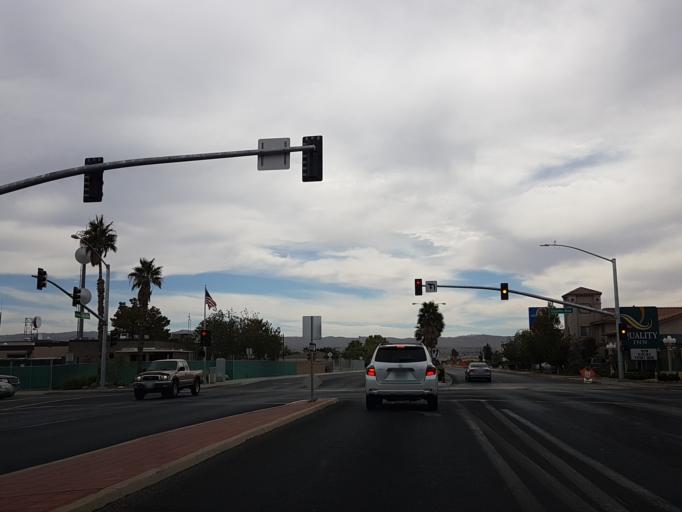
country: US
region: California
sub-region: Kern County
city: Ridgecrest
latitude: 35.6156
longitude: -117.6701
